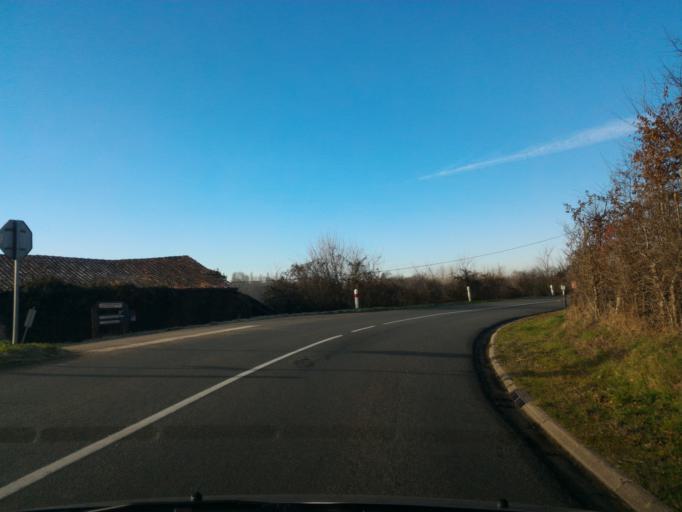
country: FR
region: Poitou-Charentes
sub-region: Departement de la Charente
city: Champagne-Mouton
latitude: 46.0241
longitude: 0.5214
